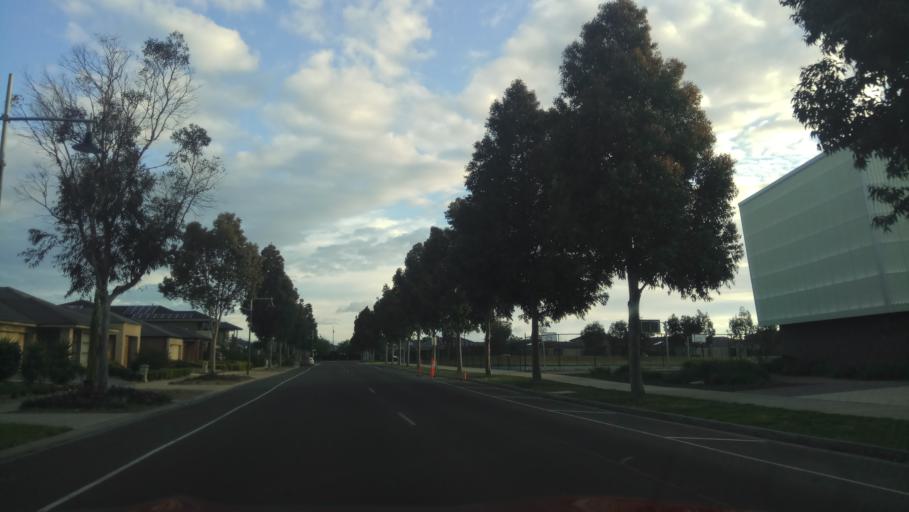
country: AU
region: Victoria
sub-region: Wyndham
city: Point Cook
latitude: -37.9087
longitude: 144.7415
